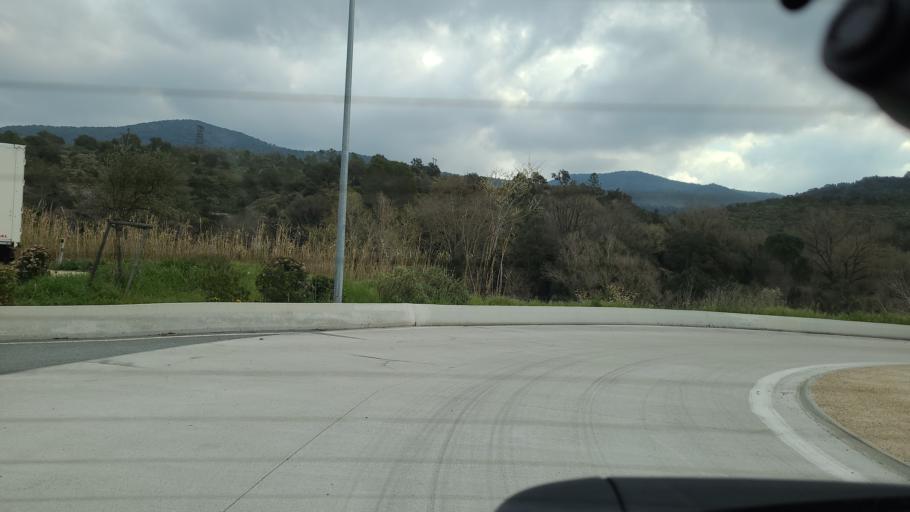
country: FR
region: Provence-Alpes-Cote d'Azur
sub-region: Departement du Var
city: Bagnols-en-Foret
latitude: 43.4997
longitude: 6.7568
